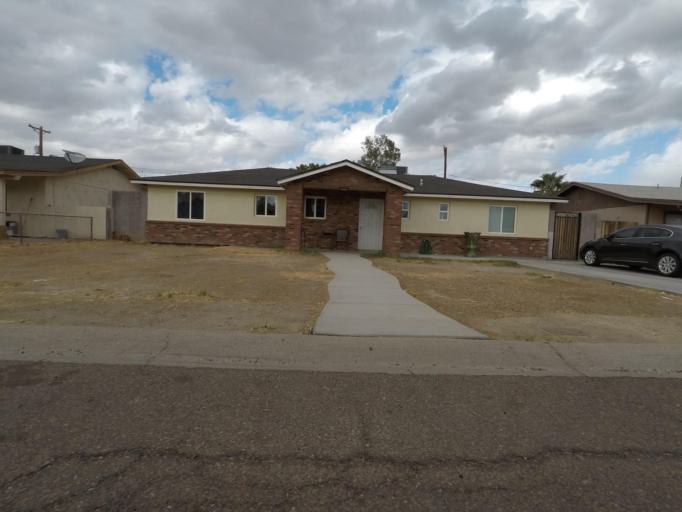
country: US
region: Arizona
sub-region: Maricopa County
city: Glendale
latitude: 33.4986
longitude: -112.1288
